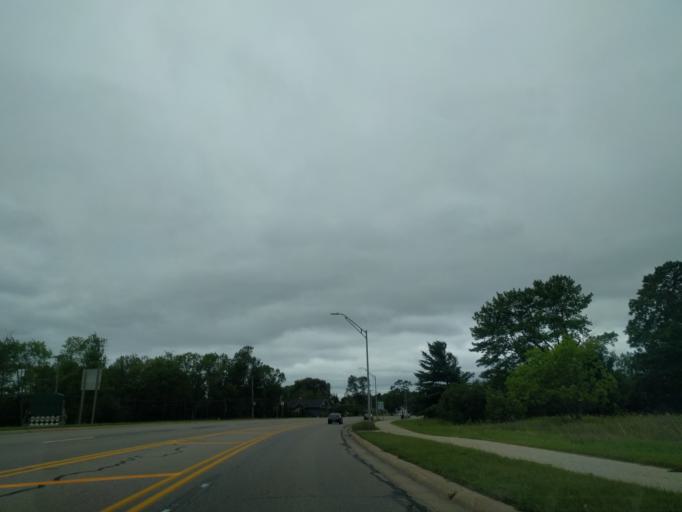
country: US
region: Michigan
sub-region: Delta County
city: Escanaba
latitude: 45.7155
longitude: -87.0817
